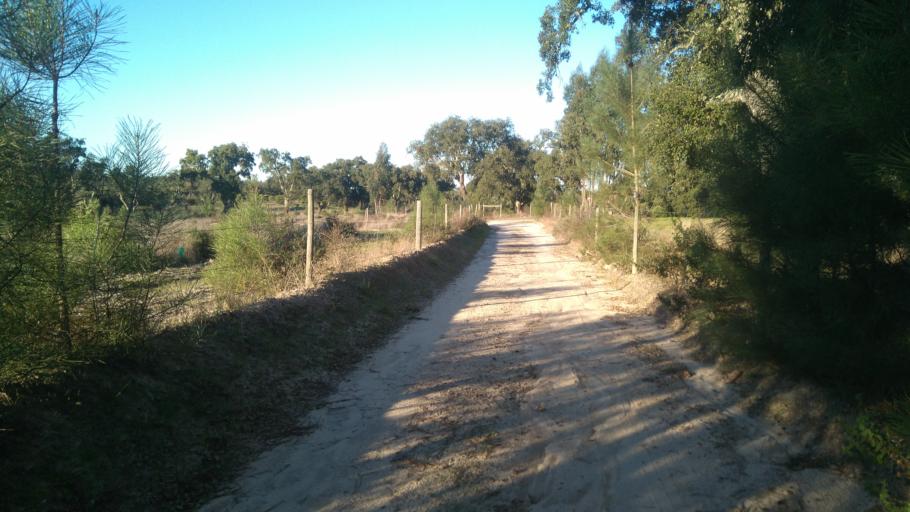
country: PT
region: Santarem
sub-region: Coruche
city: Coruche
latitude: 38.8612
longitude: -8.5258
